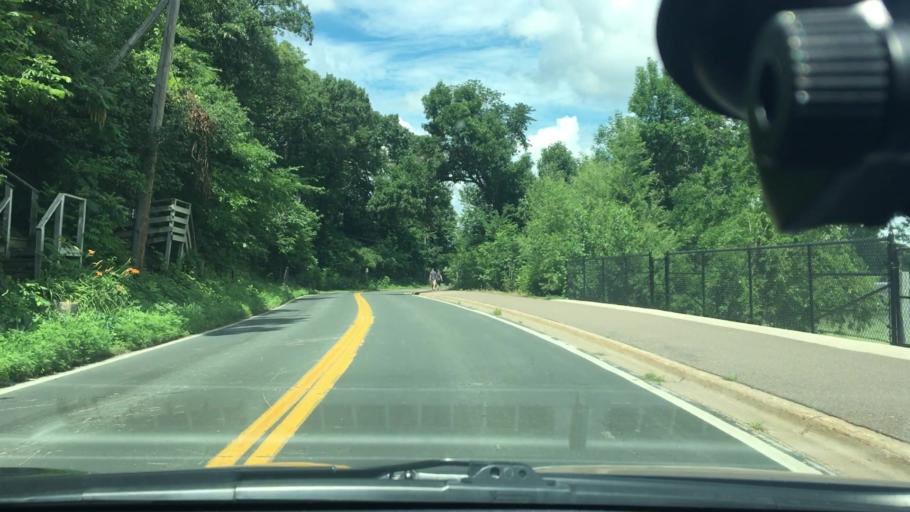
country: US
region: Minnesota
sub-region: Hennepin County
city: Plymouth
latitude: 44.9981
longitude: -93.4281
